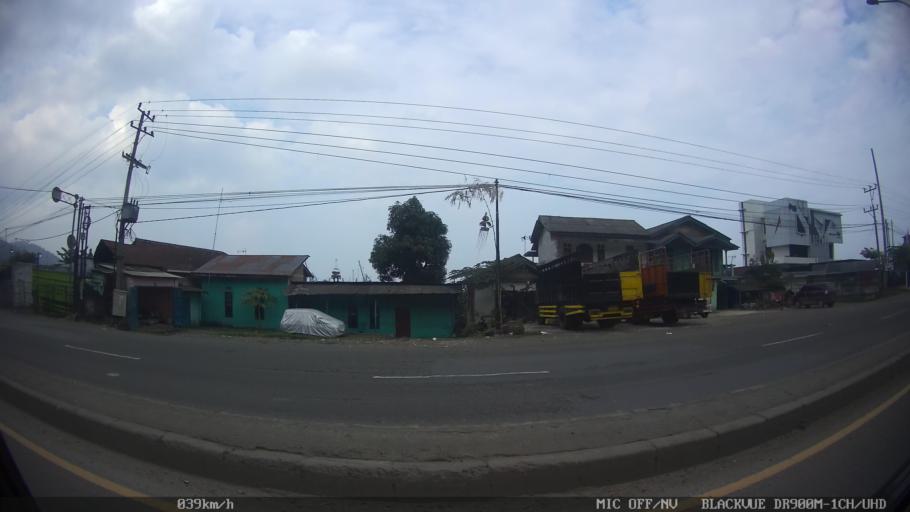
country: ID
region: Lampung
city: Panjang
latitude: -5.4603
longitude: 105.3194
